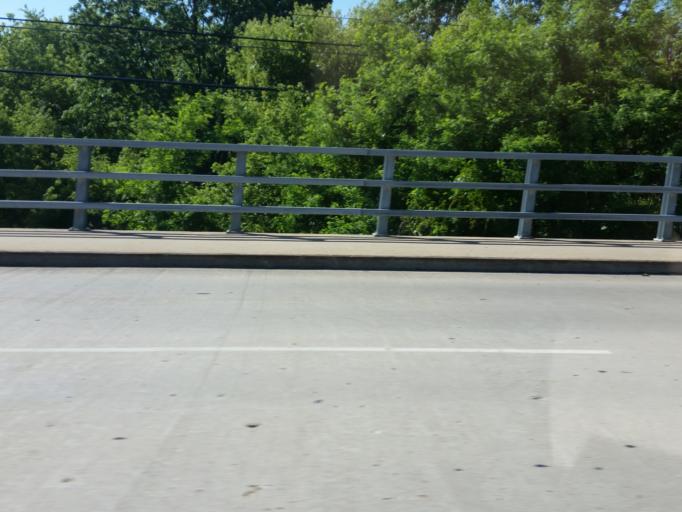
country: US
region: Wisconsin
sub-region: Rock County
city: Beloit
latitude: 42.5119
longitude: -89.0113
